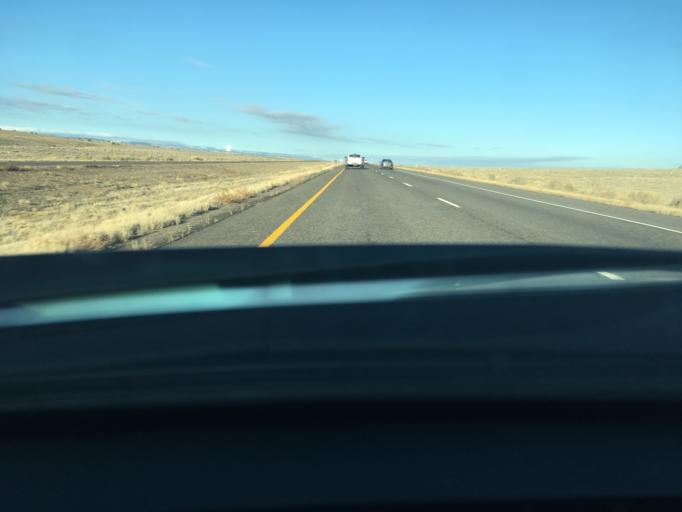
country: US
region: Colorado
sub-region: Delta County
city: Delta
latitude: 38.7793
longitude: -108.2370
